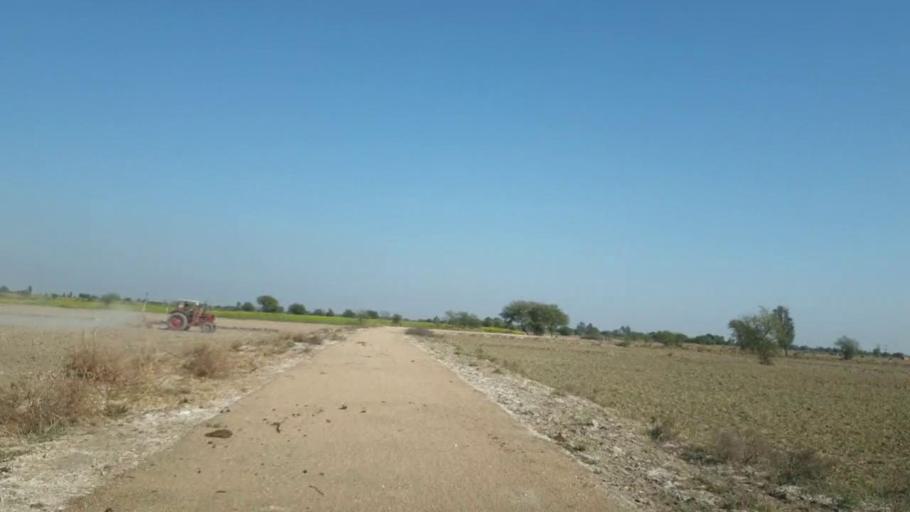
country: PK
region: Sindh
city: Mirpur Khas
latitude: 25.6275
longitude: 69.0398
